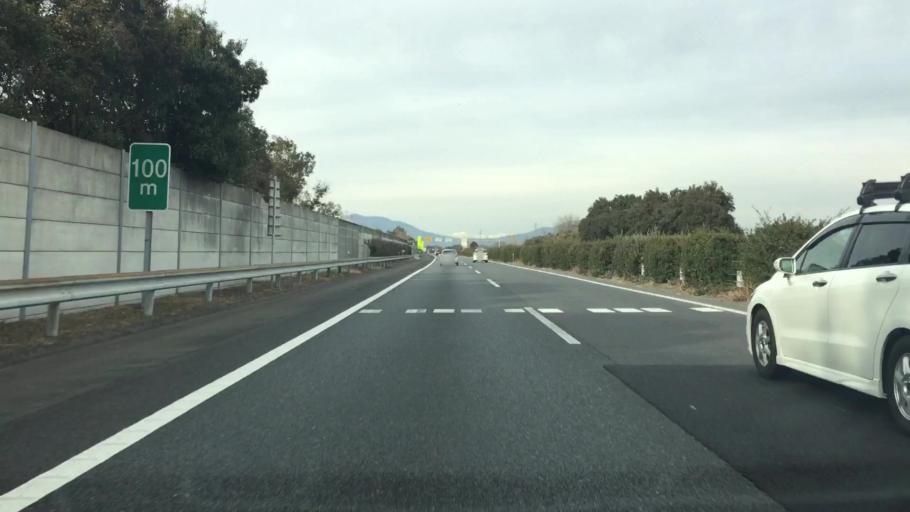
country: JP
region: Gunma
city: Kanekomachi
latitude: 36.4151
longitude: 139.0208
